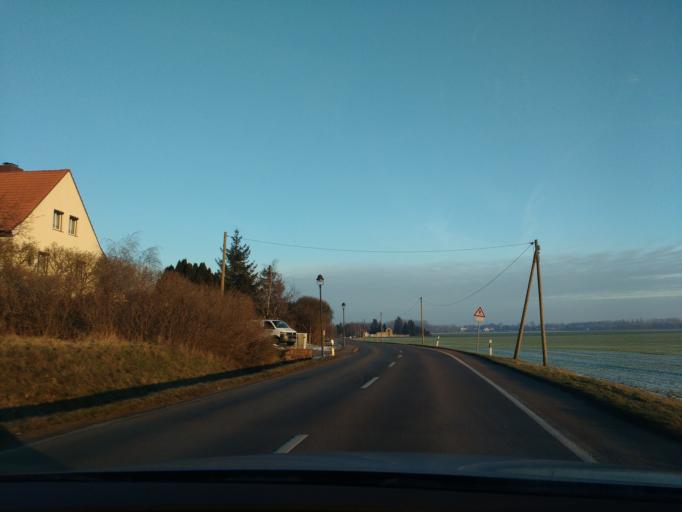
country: DE
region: Saxony-Anhalt
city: Halle (Saale)
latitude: 51.4900
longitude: 12.0225
